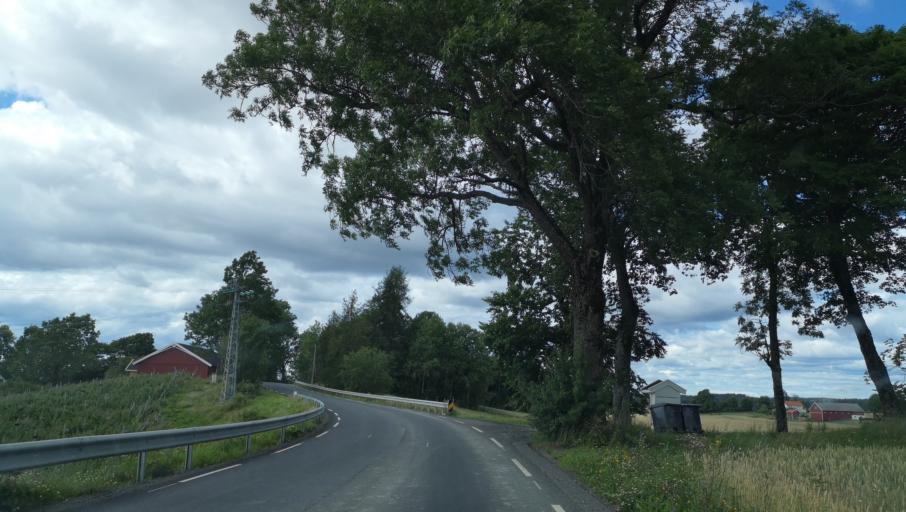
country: NO
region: Akershus
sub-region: Ski
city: Ski
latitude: 59.6939
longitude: 10.9032
